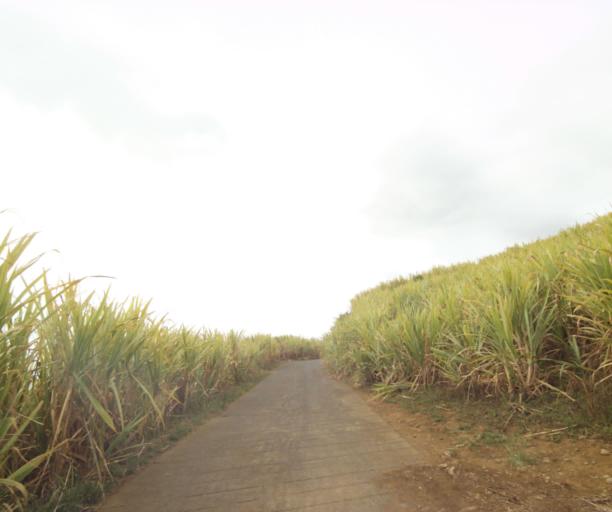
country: RE
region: Reunion
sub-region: Reunion
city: Saint-Paul
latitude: -21.0250
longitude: 55.3222
